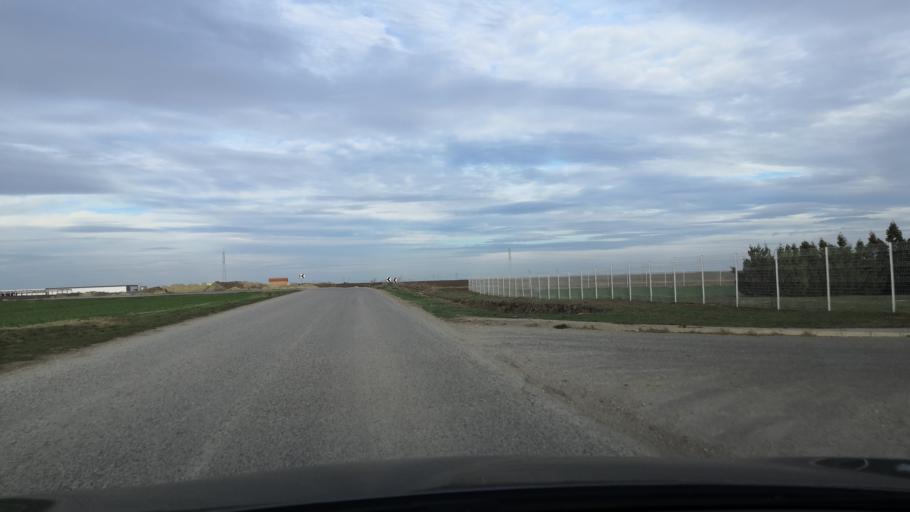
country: RS
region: Autonomna Pokrajina Vojvodina
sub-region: Sremski Okrug
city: Ingija
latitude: 45.0486
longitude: 20.1069
